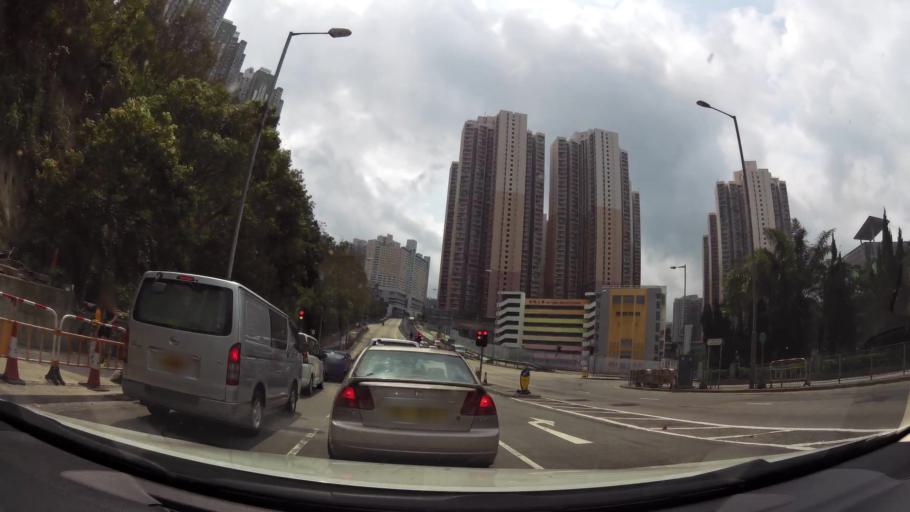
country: HK
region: Kowloon City
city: Kowloon
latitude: 22.3209
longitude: 114.2324
